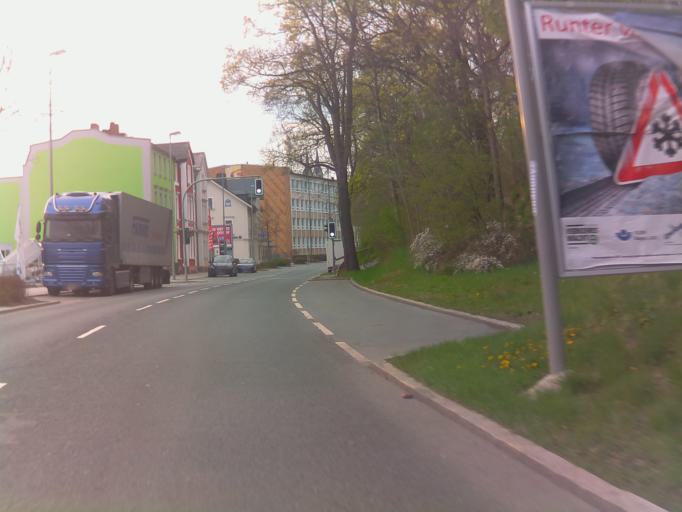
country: DE
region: Bavaria
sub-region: Upper Franconia
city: Hof
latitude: 50.3133
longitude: 11.9258
